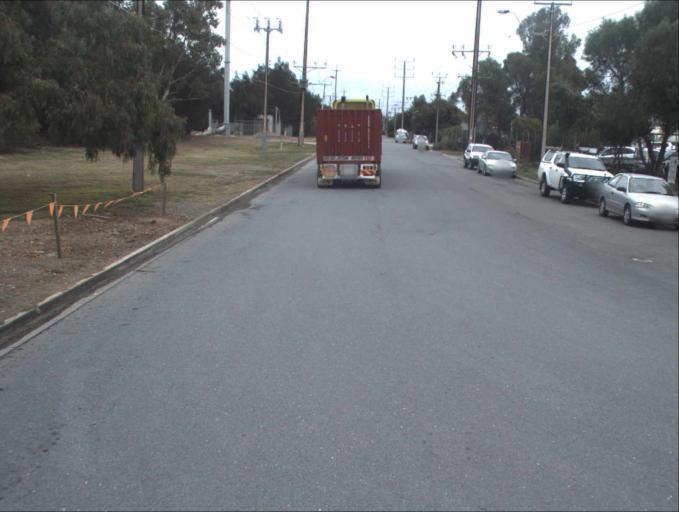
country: AU
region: South Australia
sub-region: Port Adelaide Enfield
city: Blair Athol
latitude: -34.8491
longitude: 138.5790
